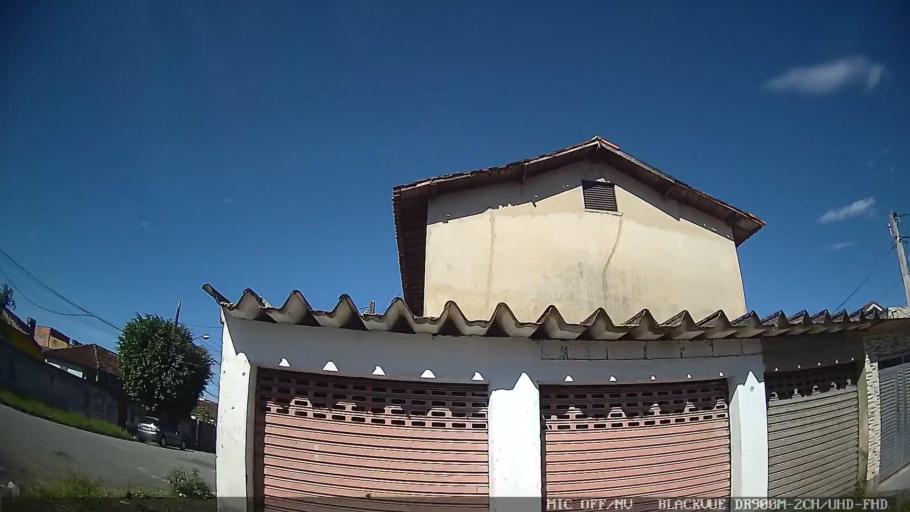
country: BR
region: Sao Paulo
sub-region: Santos
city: Santos
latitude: -23.9390
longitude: -46.2952
